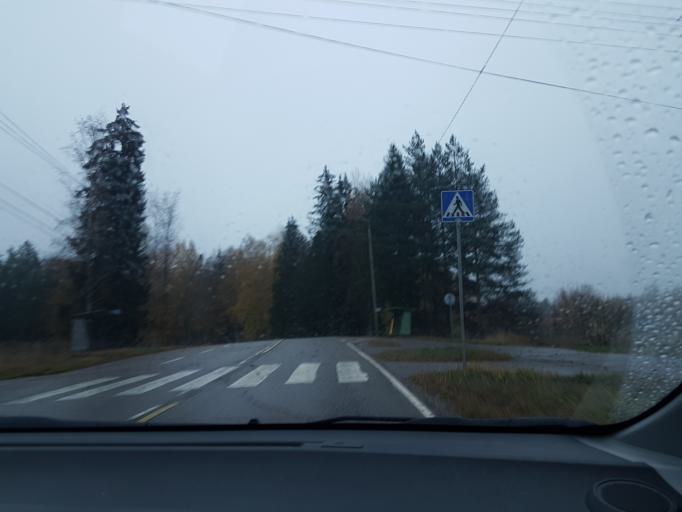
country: FI
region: Uusimaa
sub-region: Helsinki
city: Jaervenpaeae
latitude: 60.5768
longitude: 25.1596
